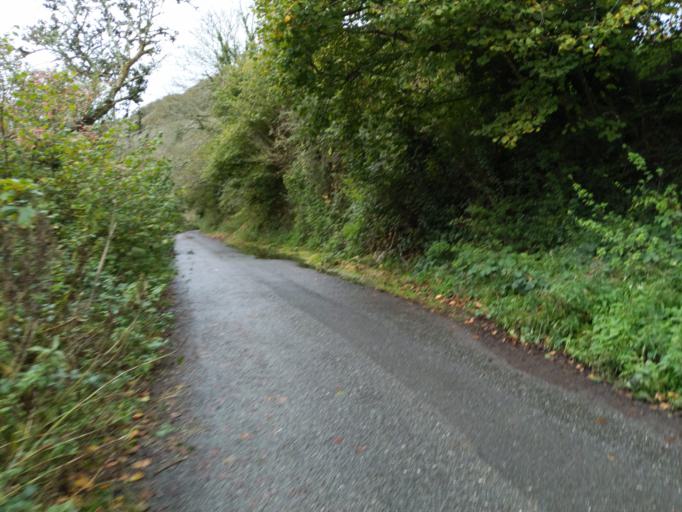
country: GB
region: England
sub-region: Plymouth
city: Plymouth
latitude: 50.4283
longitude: -4.1614
